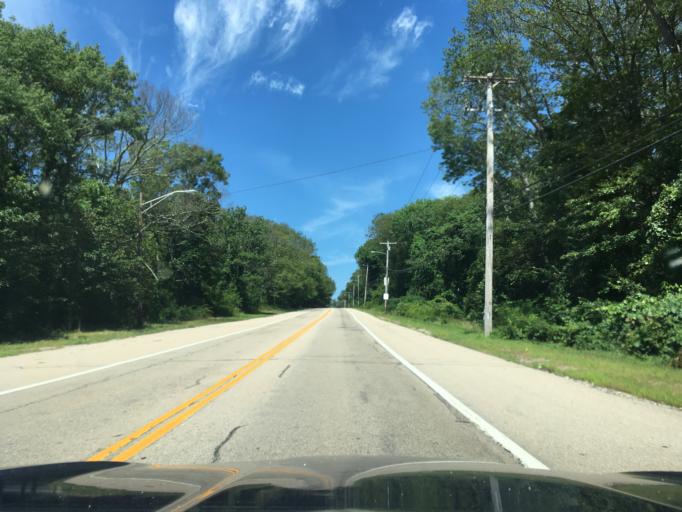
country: US
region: Rhode Island
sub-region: Kent County
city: East Greenwich
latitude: 41.6468
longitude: -71.4957
